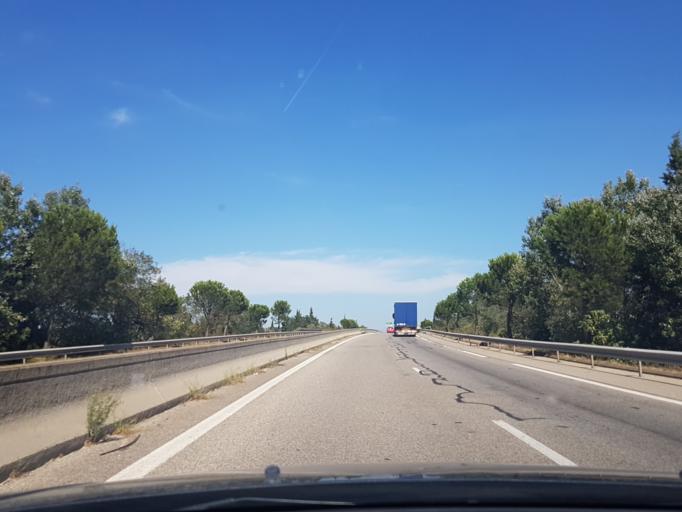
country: FR
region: Provence-Alpes-Cote d'Azur
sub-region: Departement du Vaucluse
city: Sorgues
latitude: 44.0100
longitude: 4.8640
